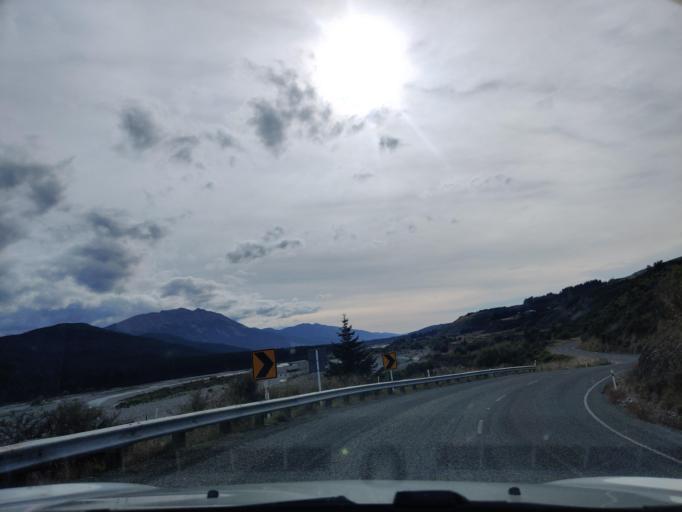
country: NZ
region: Tasman
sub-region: Tasman District
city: Wakefield
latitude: -41.6963
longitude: 173.1335
